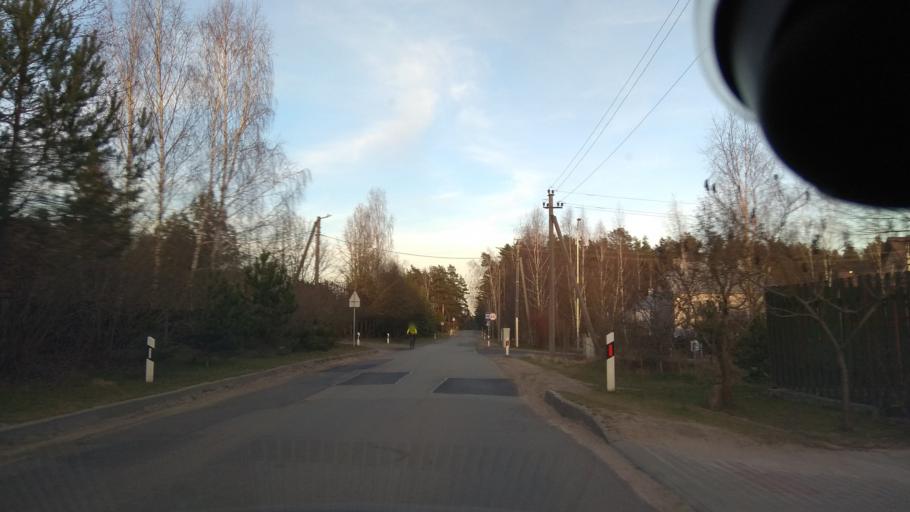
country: LT
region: Vilnius County
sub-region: Vilnius
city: Fabijoniskes
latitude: 54.7570
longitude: 25.2366
